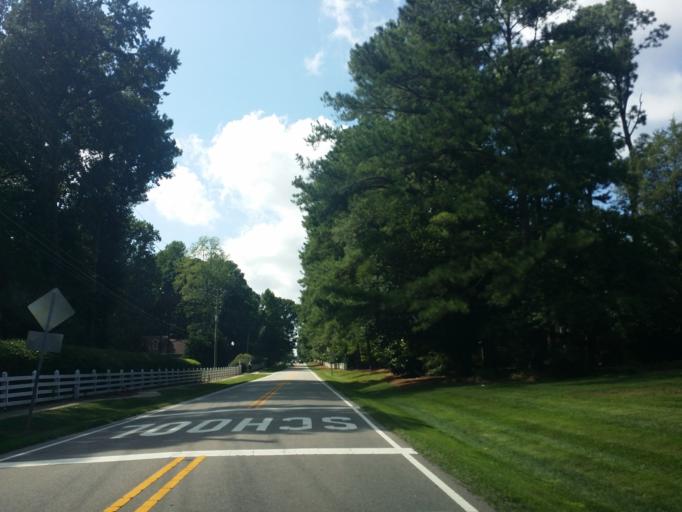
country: US
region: North Carolina
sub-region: Wake County
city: West Raleigh
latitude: 35.8939
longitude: -78.7178
